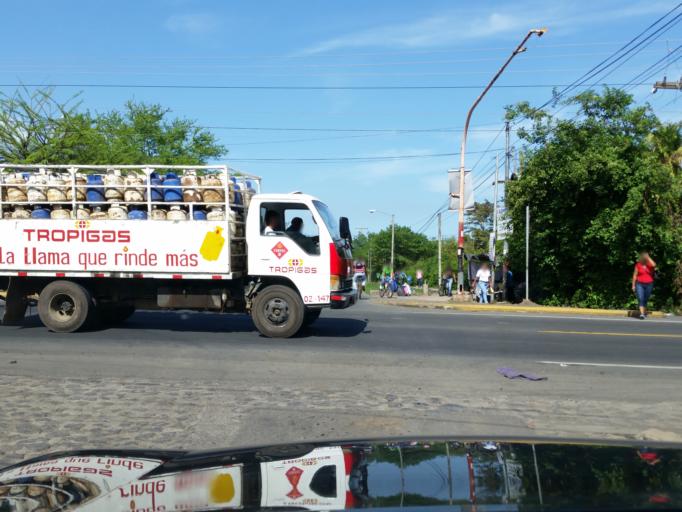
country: NI
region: Leon
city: Leon
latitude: 12.4283
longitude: -86.8650
